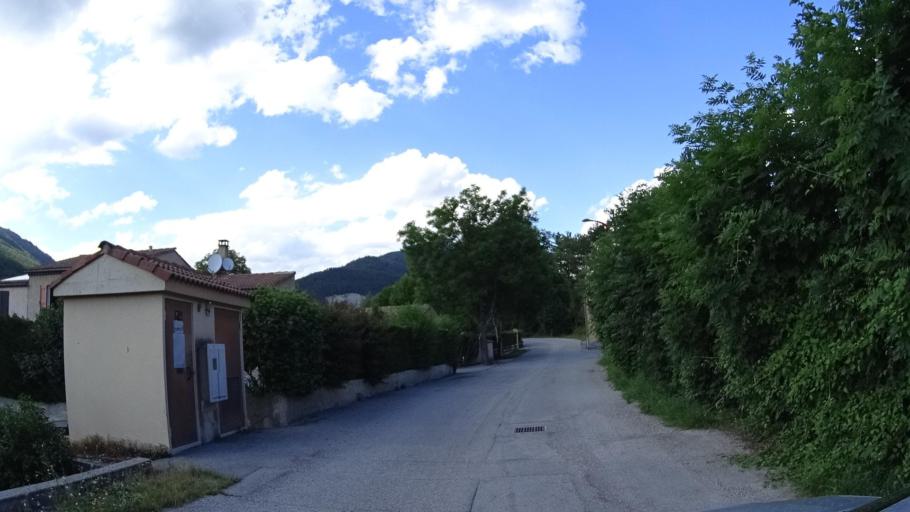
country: FR
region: Provence-Alpes-Cote d'Azur
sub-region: Departement des Alpes-de-Haute-Provence
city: Castellane
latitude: 43.9690
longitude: 6.5132
